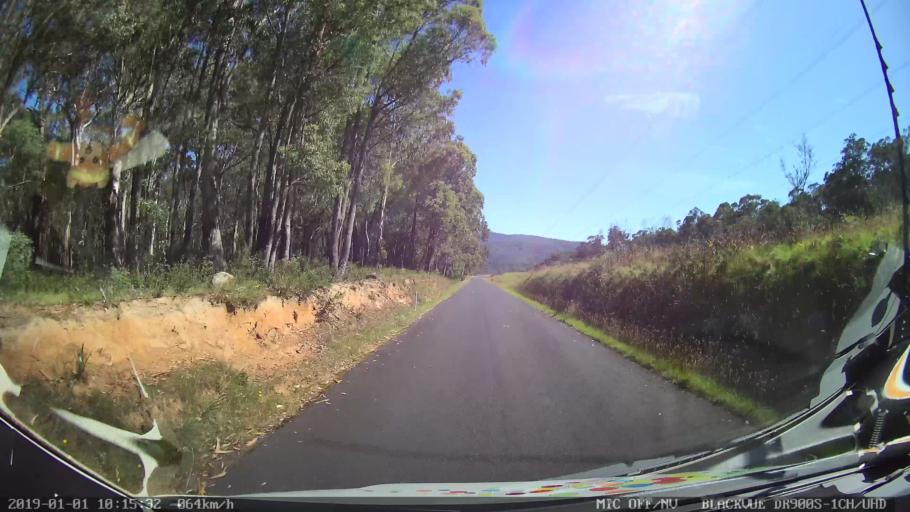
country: AU
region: New South Wales
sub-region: Snowy River
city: Jindabyne
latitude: -36.1007
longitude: 148.1621
